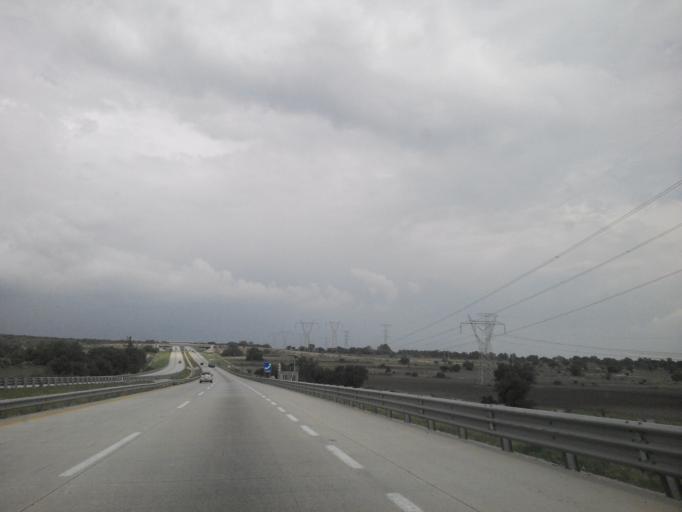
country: MX
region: Mexico
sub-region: Apaxco
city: Colonia Juarez
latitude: 19.9943
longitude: -99.1341
